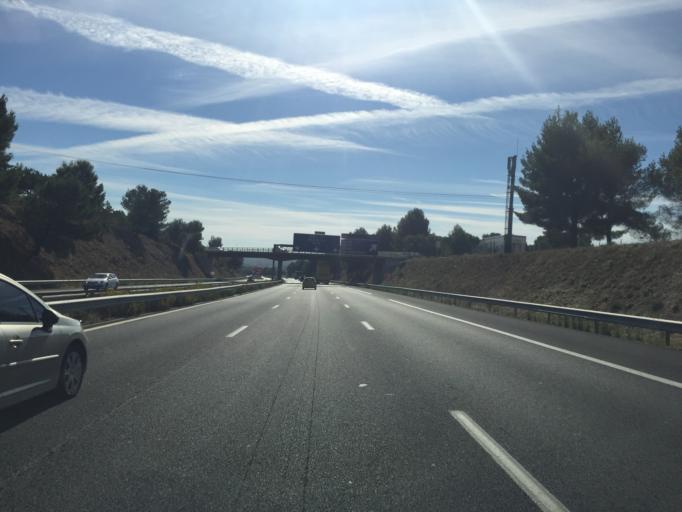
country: FR
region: Provence-Alpes-Cote d'Azur
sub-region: Departement des Bouches-du-Rhone
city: Salon-de-Provence
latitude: 43.6392
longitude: 5.1160
